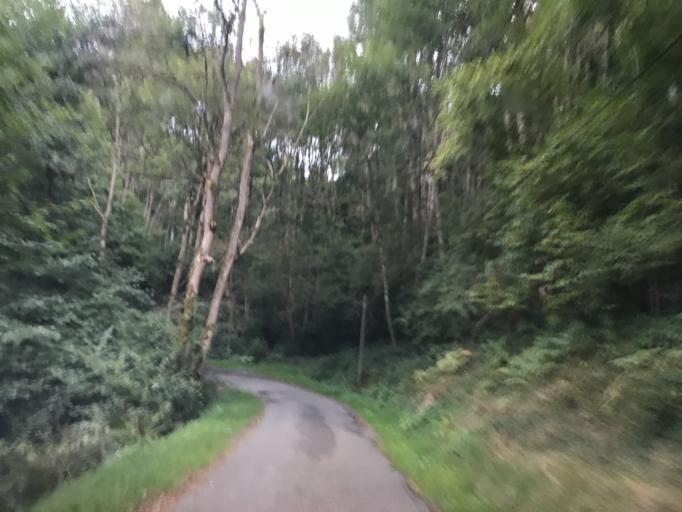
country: FR
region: Auvergne
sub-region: Departement du Puy-de-Dome
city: Thiers
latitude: 45.8472
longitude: 3.5867
